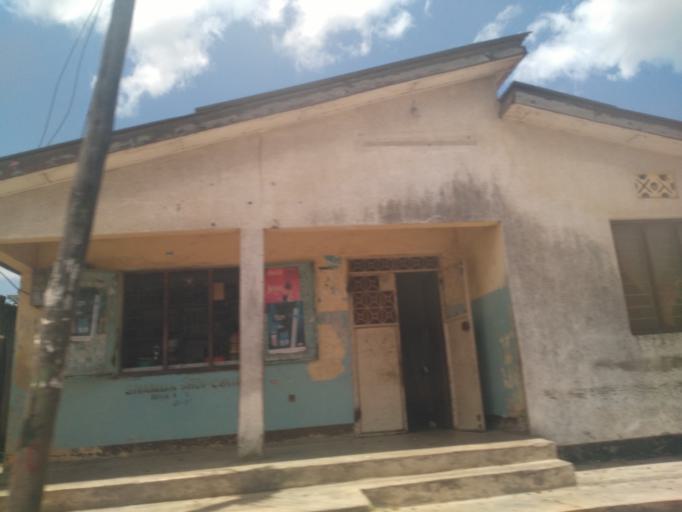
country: TZ
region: Dar es Salaam
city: Dar es Salaam
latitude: -6.8731
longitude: 39.2387
